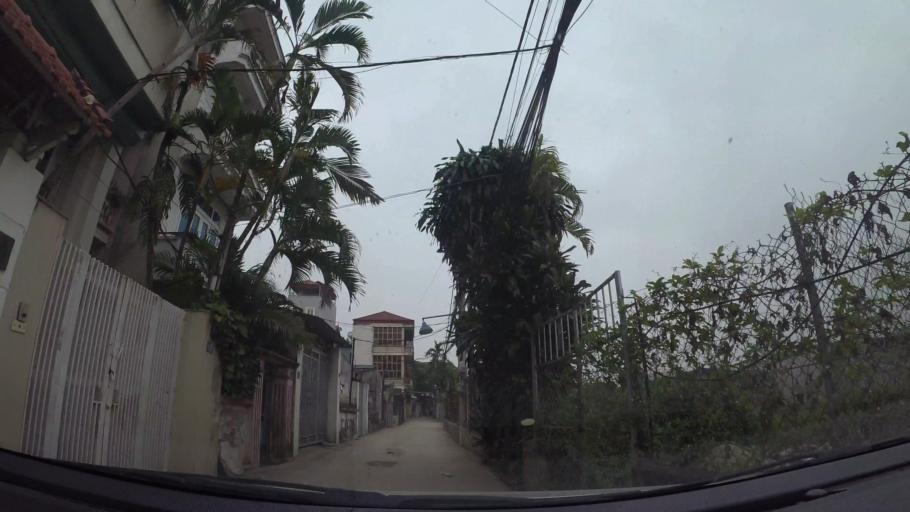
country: VN
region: Ha Noi
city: Tay Ho
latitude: 21.0827
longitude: 105.8196
